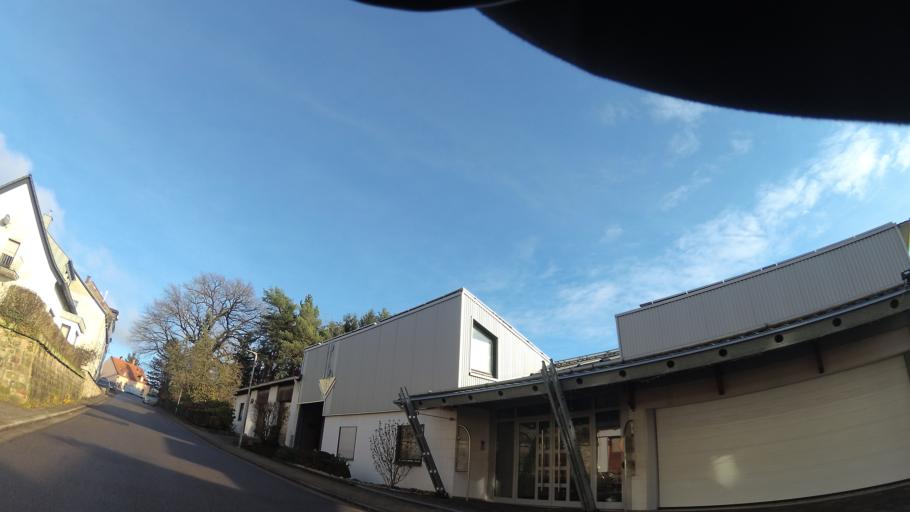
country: DE
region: Saarland
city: Spiesen-Elversberg
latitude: 49.3114
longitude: 7.1316
